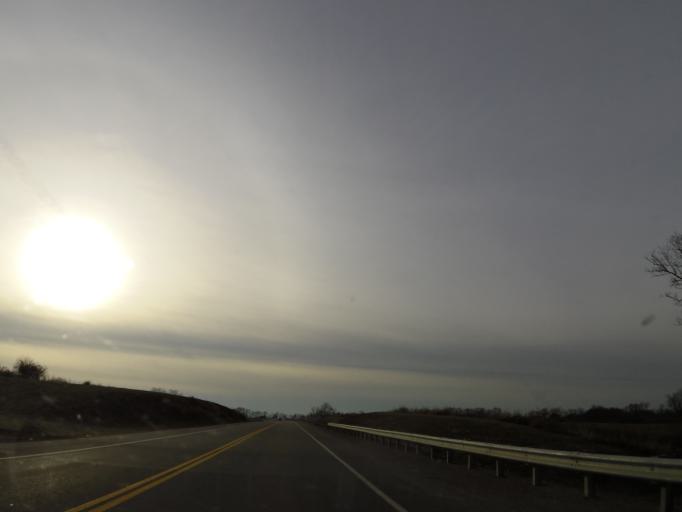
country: US
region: Kentucky
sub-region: Harrison County
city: Cynthiana
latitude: 38.3984
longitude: -84.3137
